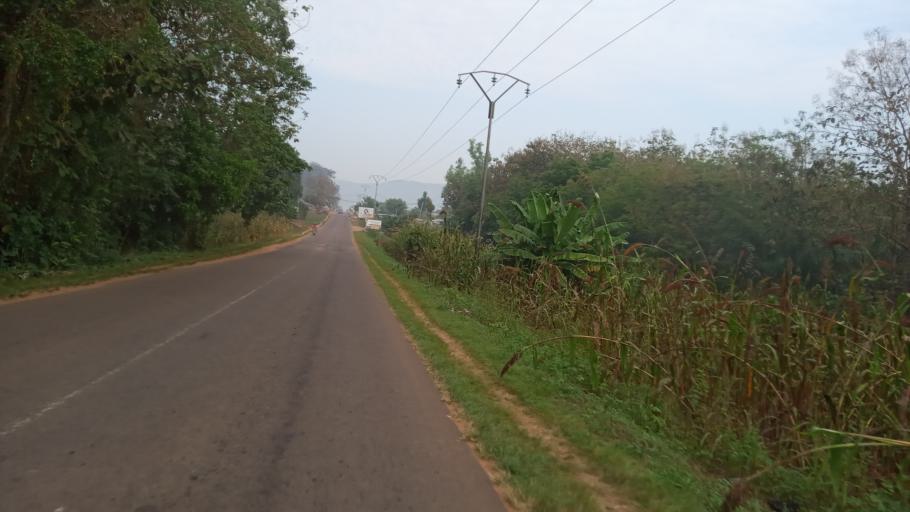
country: TG
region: Plateaux
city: Kpalime
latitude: 6.8883
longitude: 0.6432
